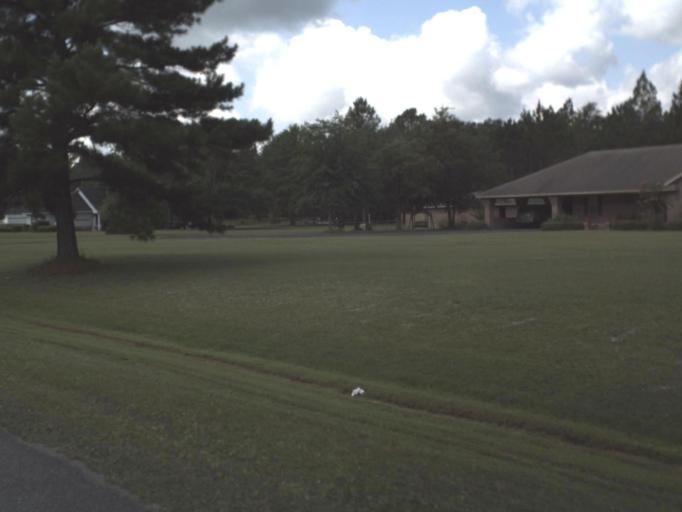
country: US
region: Florida
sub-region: Baker County
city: Macclenny
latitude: 30.3154
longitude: -82.1249
